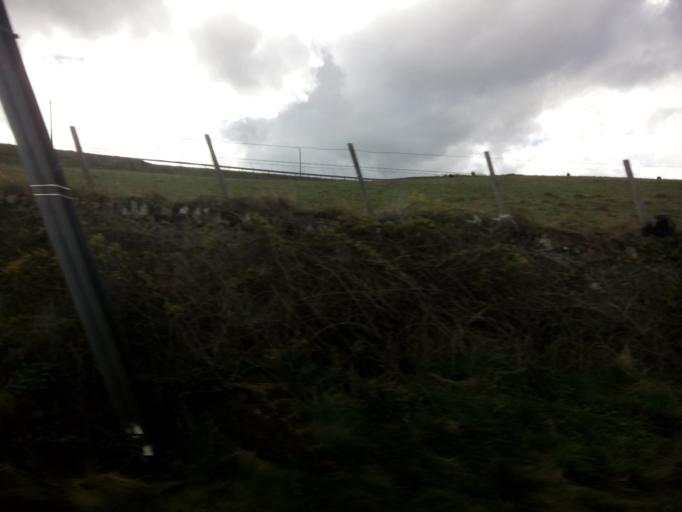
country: GB
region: Scotland
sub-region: The Scottish Borders
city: Eyemouth
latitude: 55.8383
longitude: -2.0680
